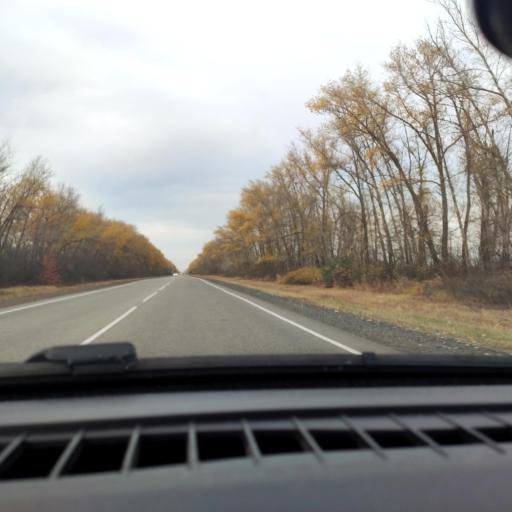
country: RU
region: Voronezj
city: Ostrogozhsk
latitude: 50.9800
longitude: 38.9944
